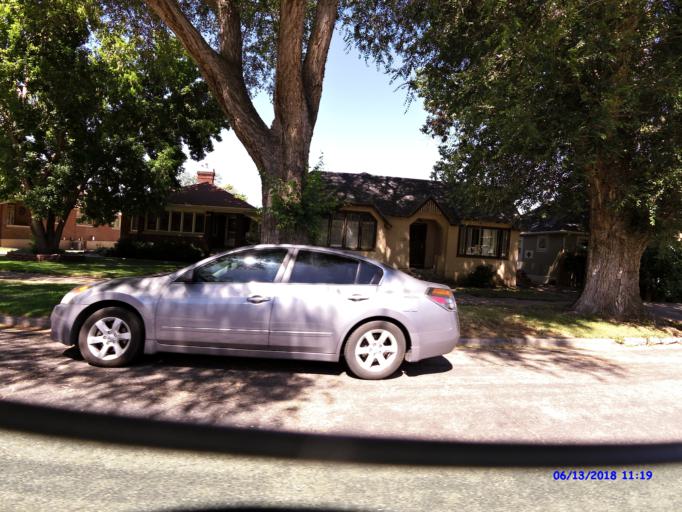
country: US
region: Utah
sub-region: Weber County
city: Ogden
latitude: 41.2199
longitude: -111.9497
